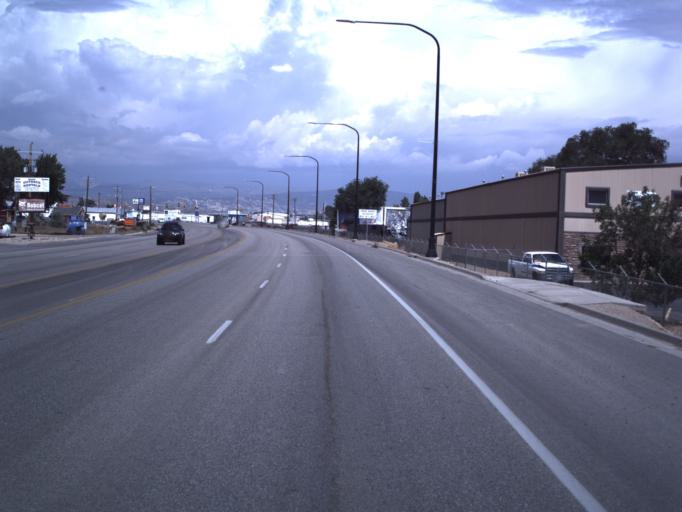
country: US
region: Utah
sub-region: Uintah County
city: Naples
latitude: 40.4460
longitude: -109.5003
